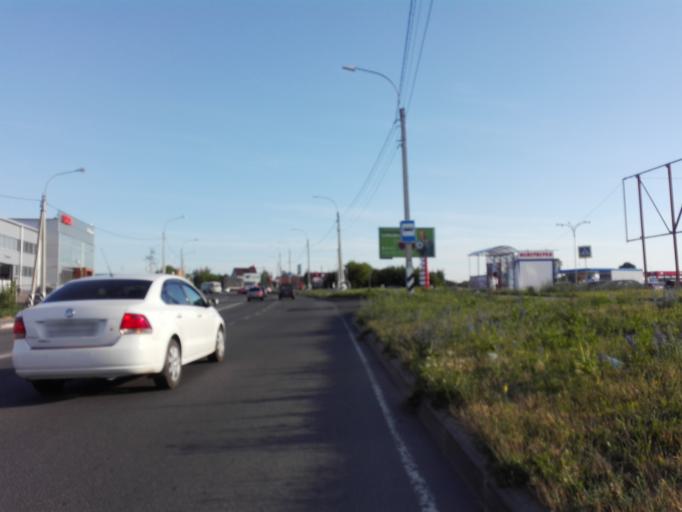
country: RU
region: Orjol
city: Orel
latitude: 52.9485
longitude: 36.0240
